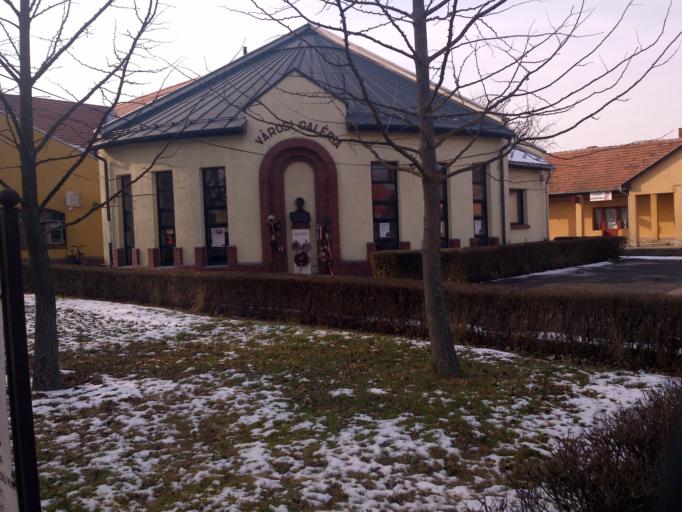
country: HU
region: Borsod-Abauj-Zemplen
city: Encs
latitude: 48.3315
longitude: 21.1193
